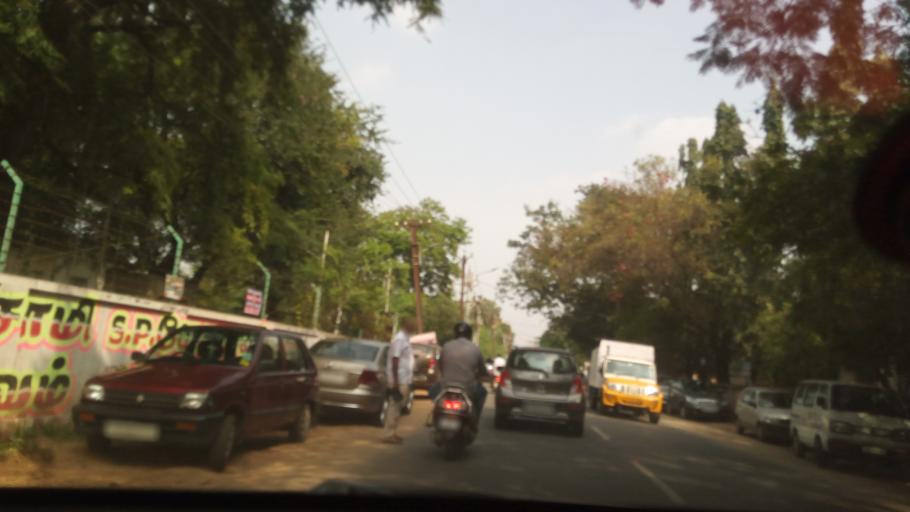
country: IN
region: Tamil Nadu
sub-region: Coimbatore
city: Coimbatore
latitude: 11.0149
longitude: 76.9479
